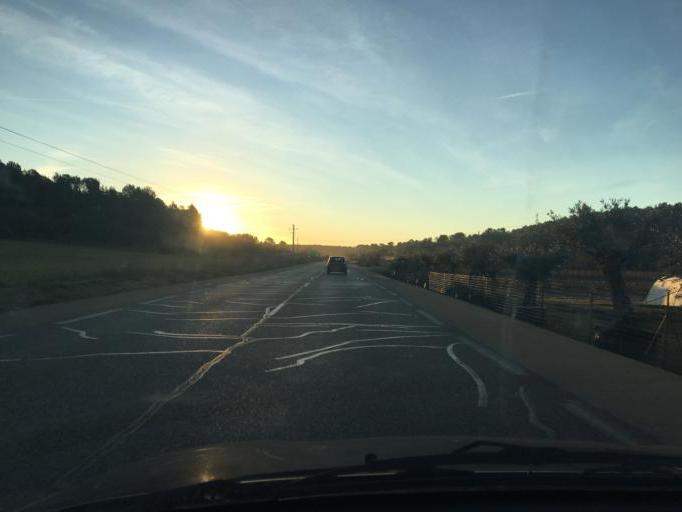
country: FR
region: Provence-Alpes-Cote d'Azur
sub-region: Departement du Var
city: Lorgues
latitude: 43.4746
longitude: 6.3763
